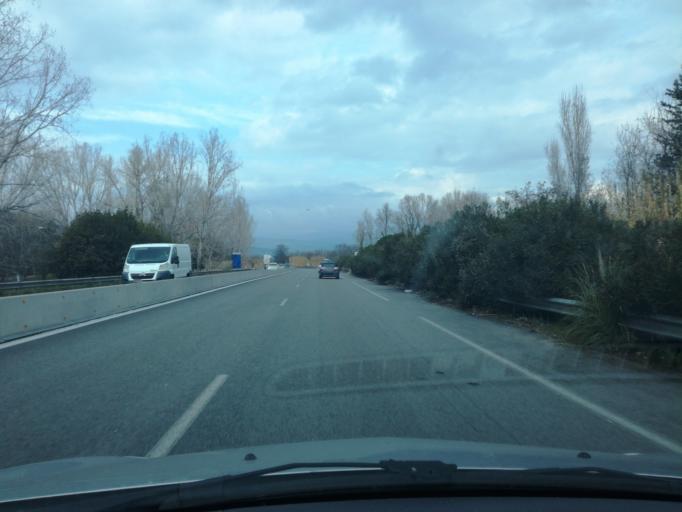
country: FR
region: Provence-Alpes-Cote d'Azur
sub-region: Departement des Alpes-Maritimes
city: Mandelieu-la-Napoule
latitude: 43.5591
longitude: 6.9547
